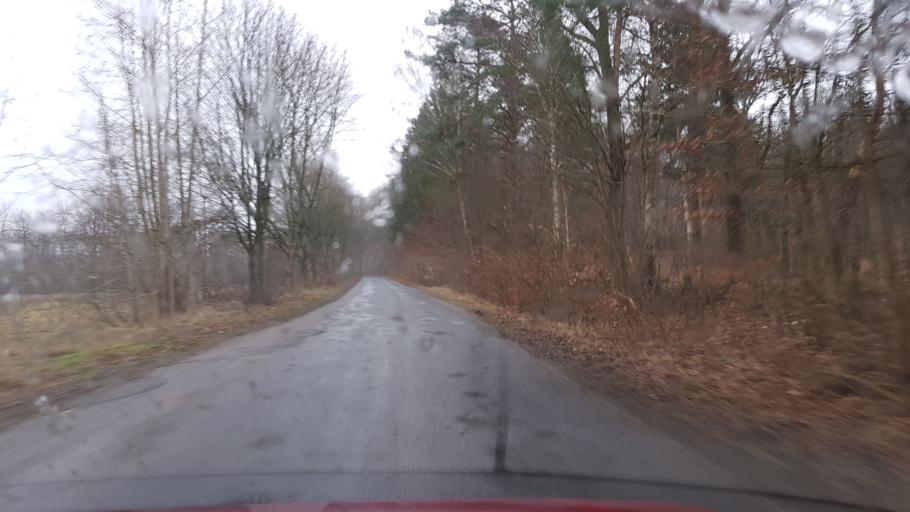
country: PL
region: West Pomeranian Voivodeship
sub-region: Powiat slawienski
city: Slawno
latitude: 54.2659
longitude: 16.5584
